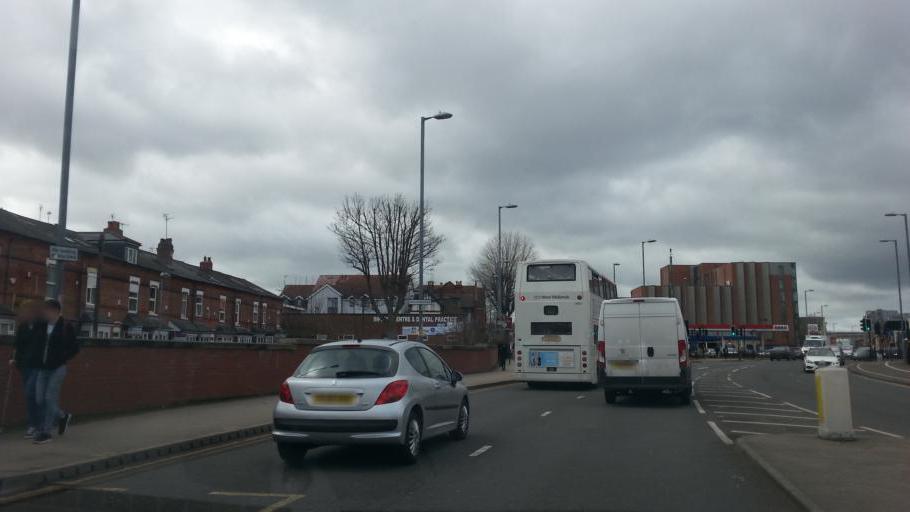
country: GB
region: England
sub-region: City and Borough of Birmingham
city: Birmingham
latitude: 52.4470
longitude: -1.9285
